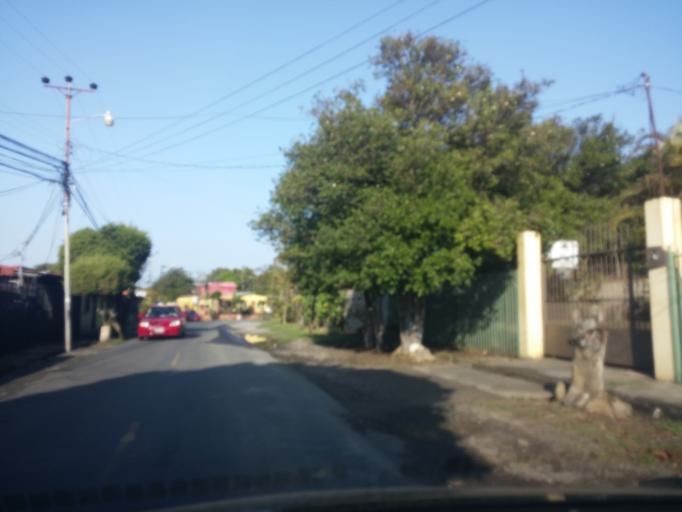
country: CR
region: Heredia
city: Llorente
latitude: 10.0055
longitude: -84.1459
